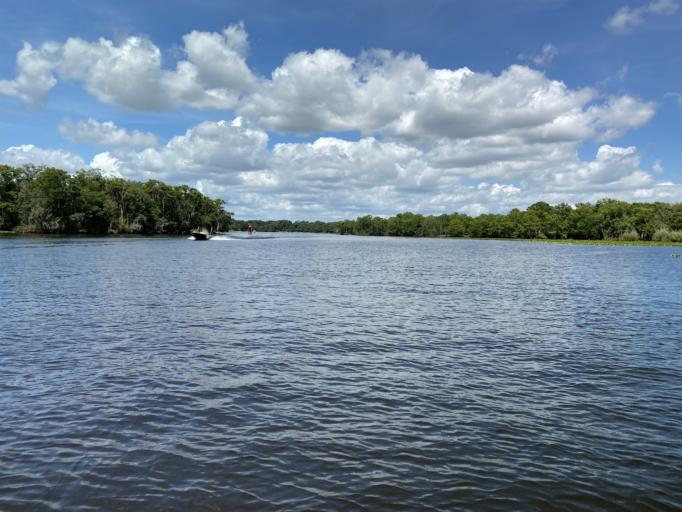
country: US
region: Florida
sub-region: Volusia County
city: DeBary
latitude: 28.8522
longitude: -81.3576
